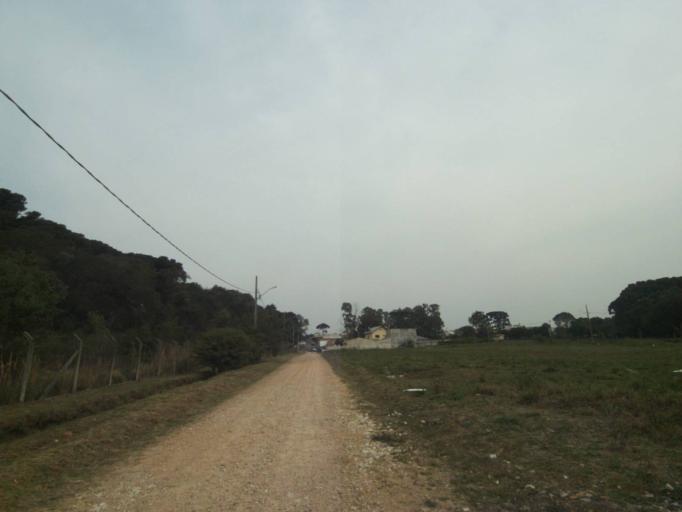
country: BR
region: Parana
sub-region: Sao Jose Dos Pinhais
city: Sao Jose dos Pinhais
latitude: -25.5238
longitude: -49.2770
